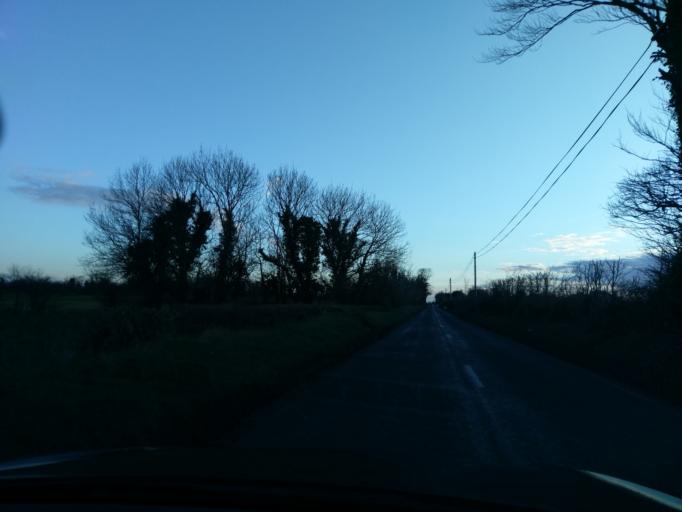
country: IE
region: Connaught
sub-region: County Galway
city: Athenry
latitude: 53.2984
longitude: -8.6278
